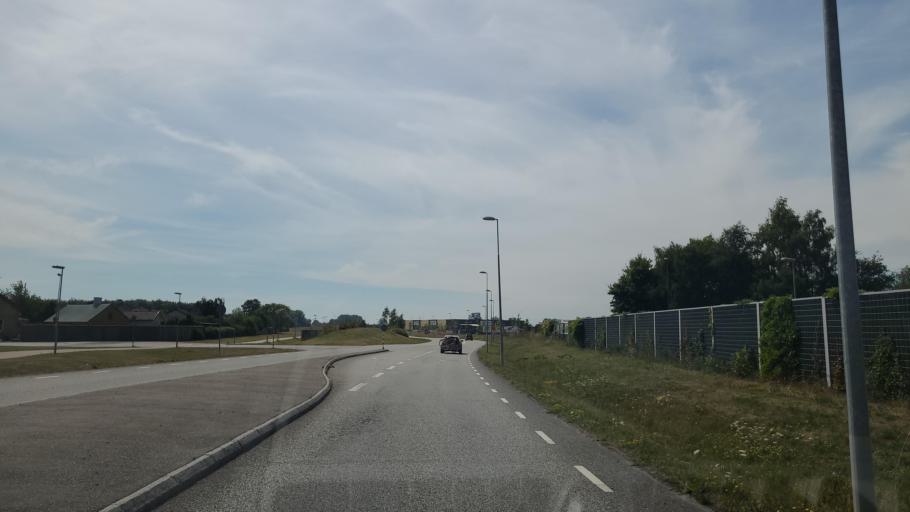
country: SE
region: Skane
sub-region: Trelleborgs Kommun
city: Trelleborg
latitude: 55.3866
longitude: 13.1312
